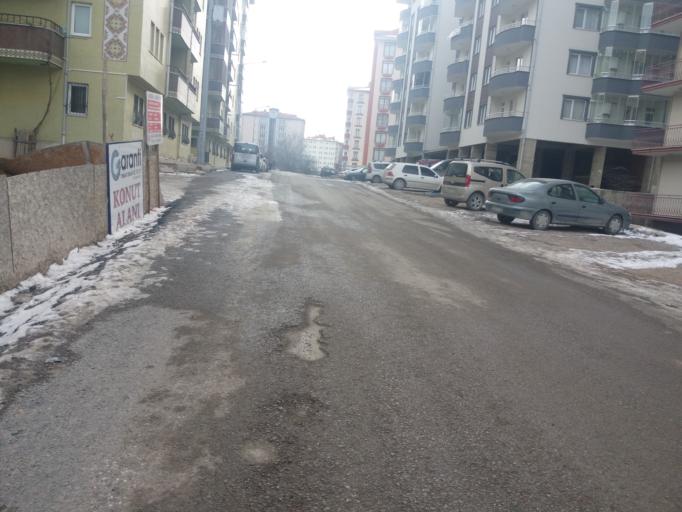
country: TR
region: Gumushane
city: Gumushkhane
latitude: 40.4545
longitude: 39.4908
